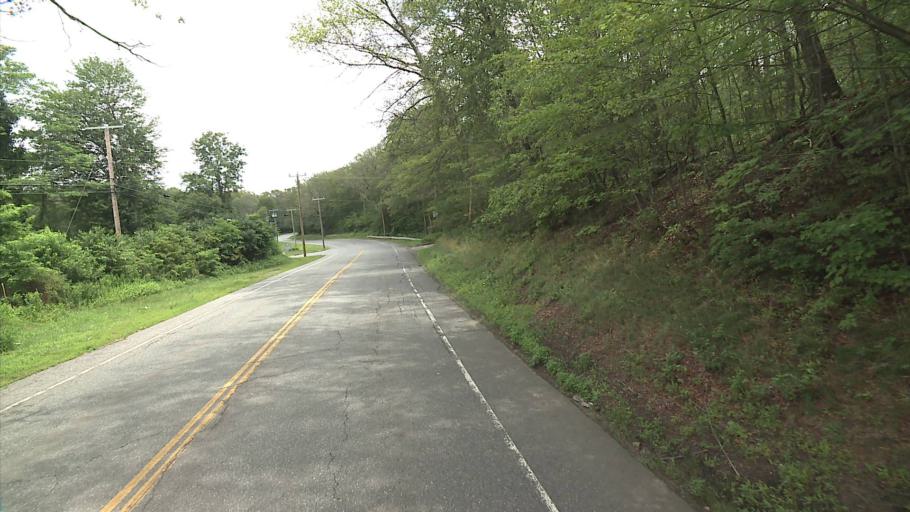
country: US
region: Connecticut
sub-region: Middlesex County
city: Deep River Center
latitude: 41.3643
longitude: -72.4738
